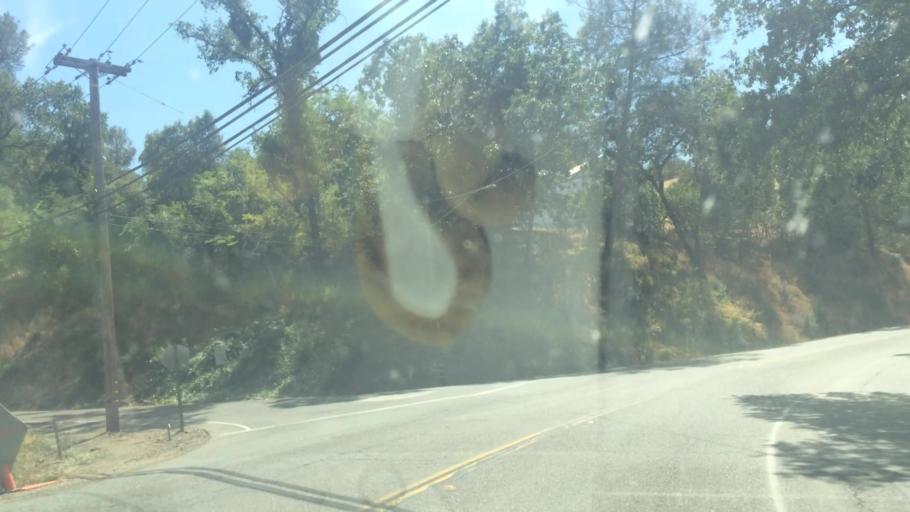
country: US
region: California
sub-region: Amador County
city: Sutter Creek
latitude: 38.3887
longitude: -120.8010
